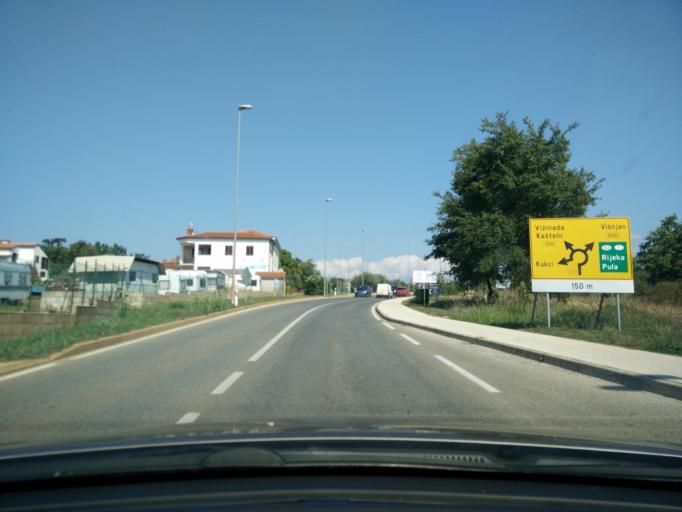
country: HR
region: Istarska
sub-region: Grad Porec
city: Porec
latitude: 45.2587
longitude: 13.6287
